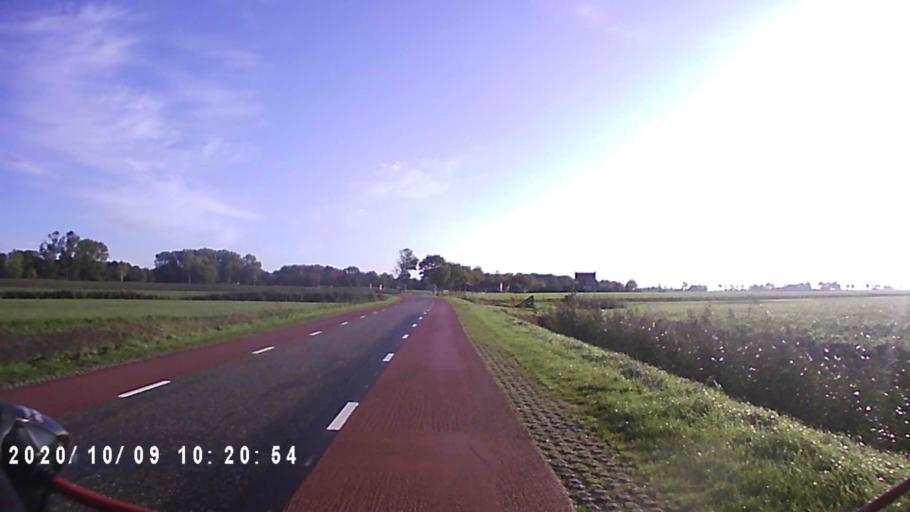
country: NL
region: Groningen
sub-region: Gemeente Winsum
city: Winsum
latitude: 53.3224
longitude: 6.5100
